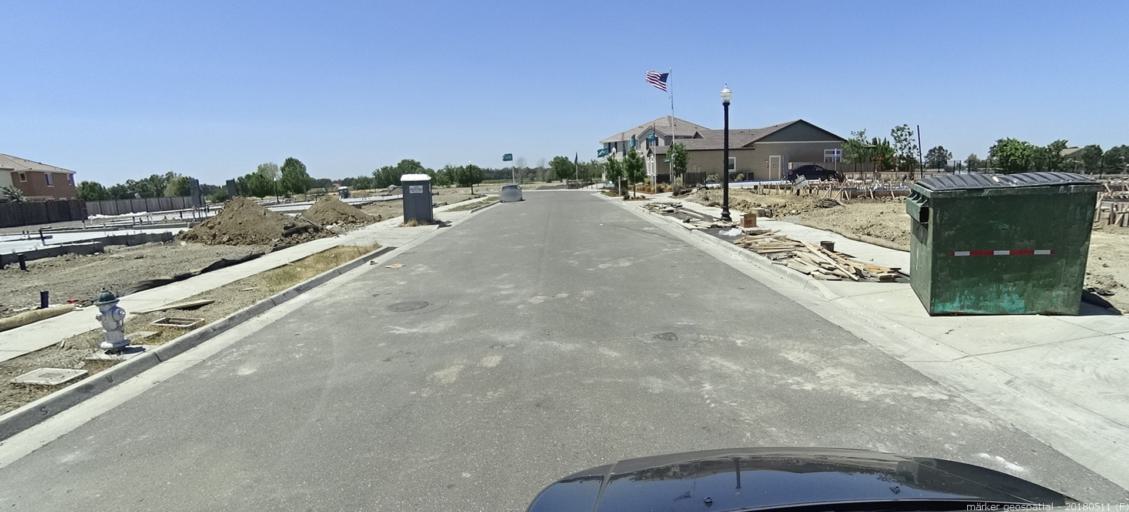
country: US
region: California
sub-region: Yolo County
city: West Sacramento
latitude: 38.6485
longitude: -121.5520
